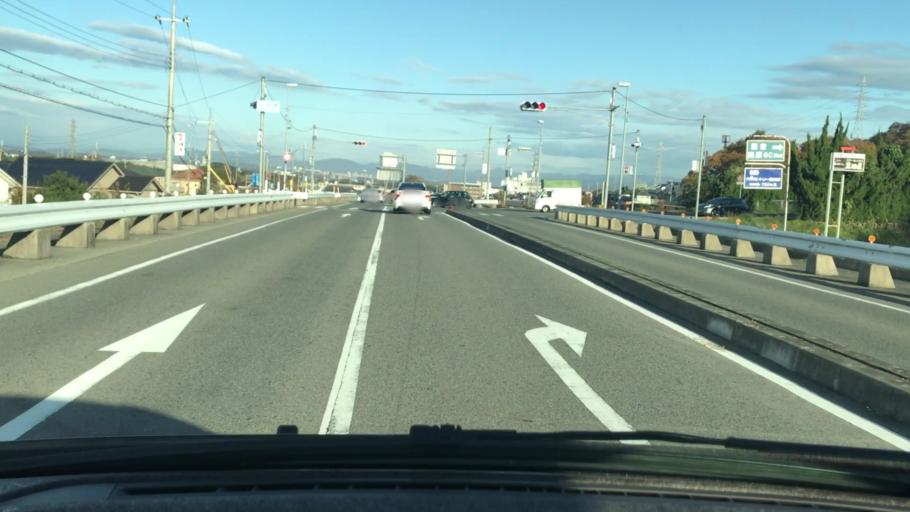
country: JP
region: Hyogo
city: Sandacho
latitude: 34.8189
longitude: 135.2492
